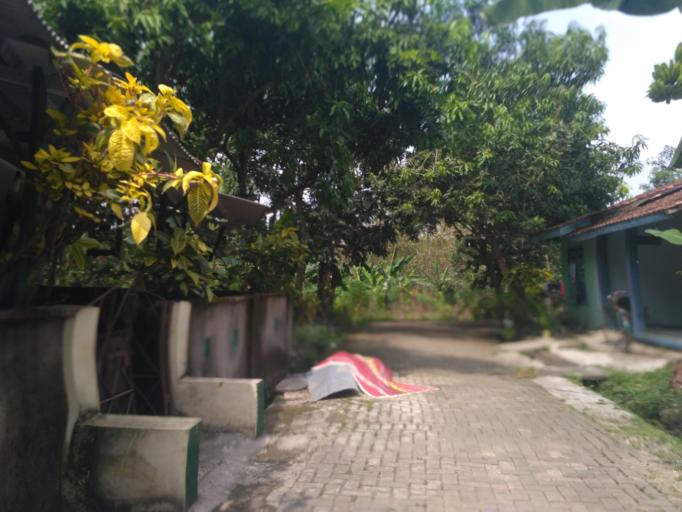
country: ID
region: Central Java
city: Mranggen
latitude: -7.0672
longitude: 110.4659
